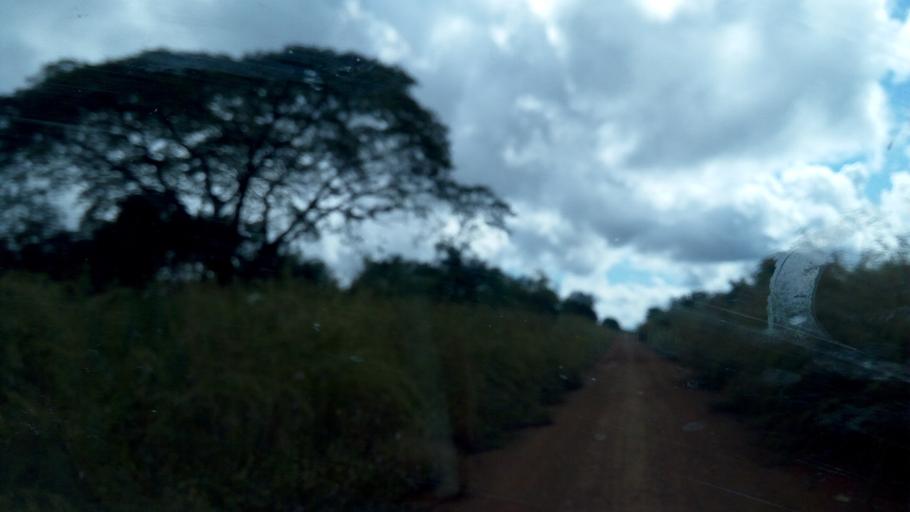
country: ZM
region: Northern
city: Kaputa
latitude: -8.3761
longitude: 28.9604
